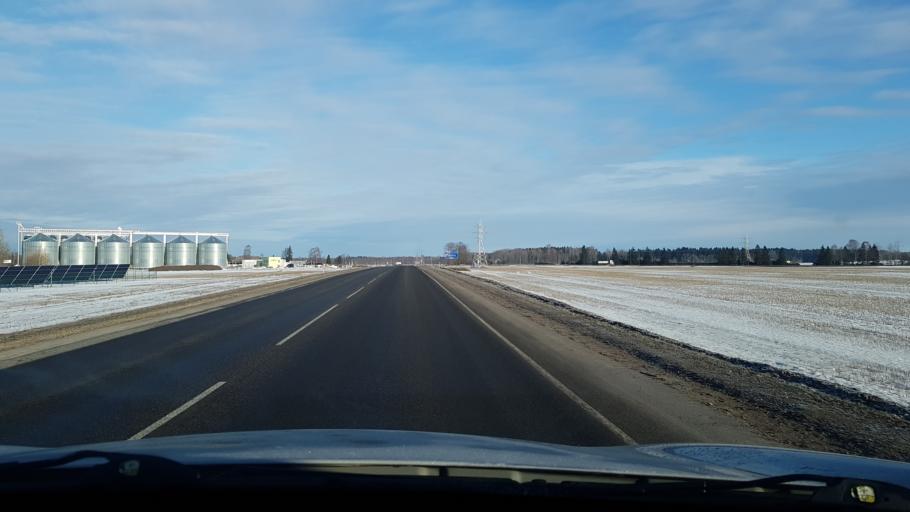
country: EE
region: Jogevamaa
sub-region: Poltsamaa linn
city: Poltsamaa
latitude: 58.7404
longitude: 25.7685
